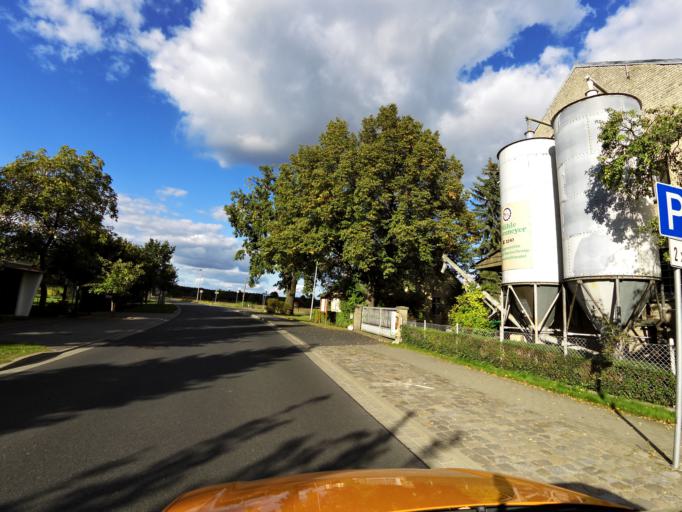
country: DE
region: Brandenburg
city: Luckenwalde
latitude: 52.1046
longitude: 13.1747
